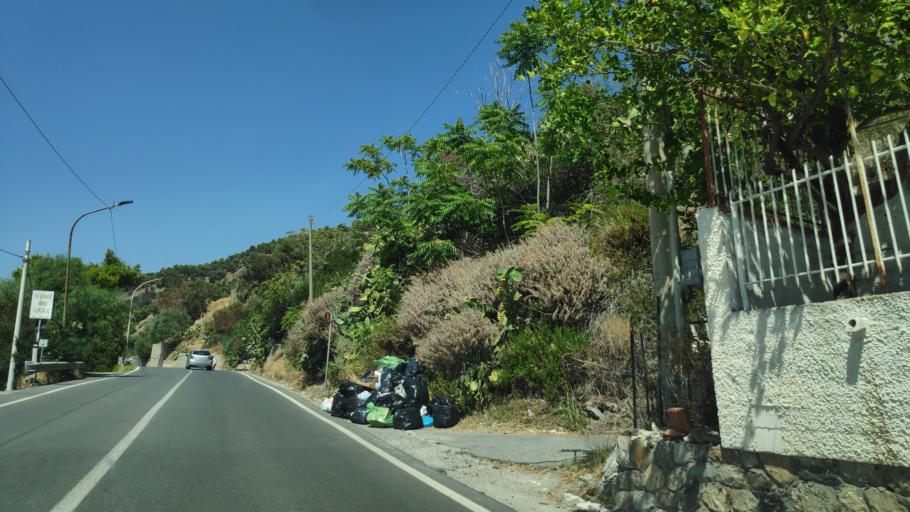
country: IT
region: Calabria
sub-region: Provincia di Reggio Calabria
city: Palizzi Marina
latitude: 37.9198
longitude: 15.9768
